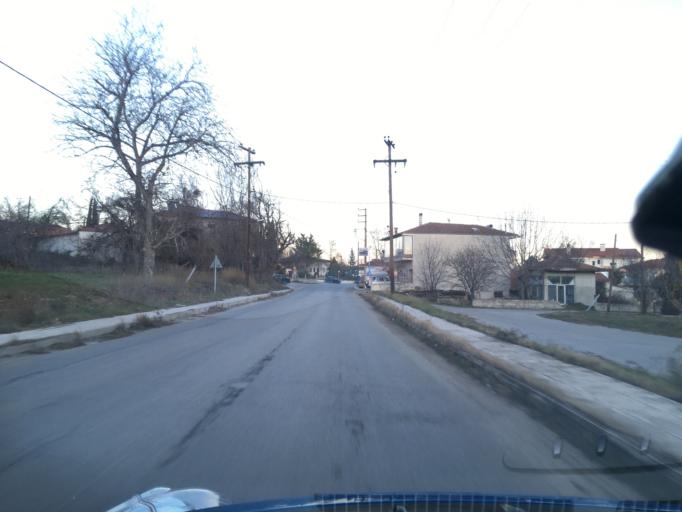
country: GR
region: West Macedonia
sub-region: Nomos Kozanis
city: Kozani
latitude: 40.2703
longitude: 21.7757
